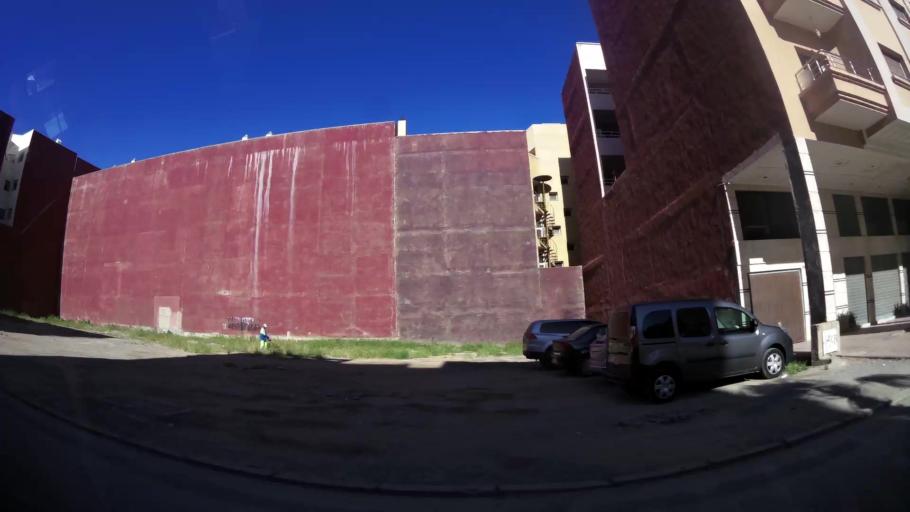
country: MA
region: Oriental
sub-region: Oujda-Angad
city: Oujda
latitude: 34.6606
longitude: -1.8989
